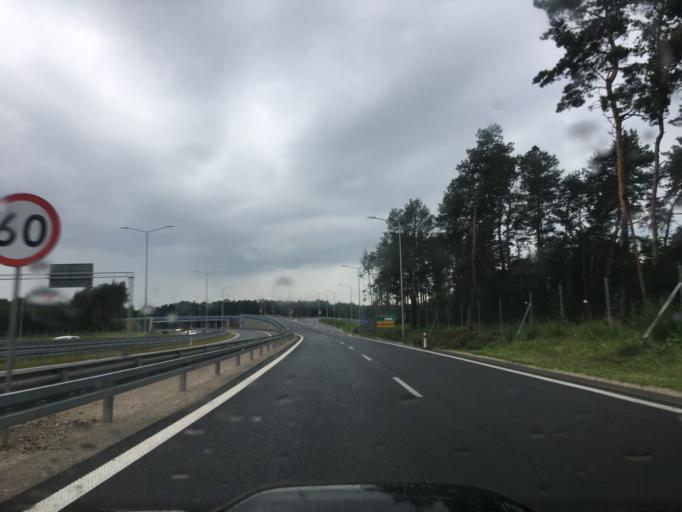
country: PL
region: Masovian Voivodeship
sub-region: Powiat piaseczynski
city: Gora Kalwaria
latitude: 51.9702
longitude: 21.2006
